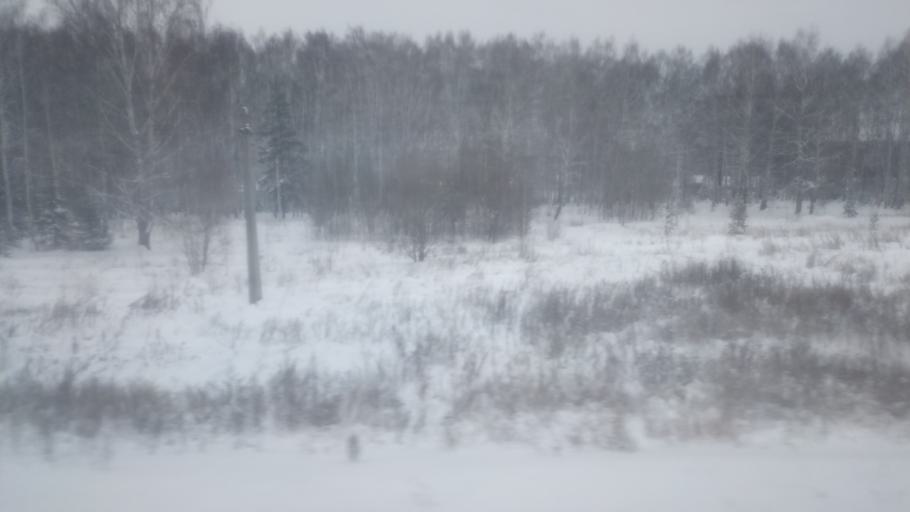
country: RU
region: Udmurtiya
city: Malaya Purga
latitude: 56.5557
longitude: 53.1227
